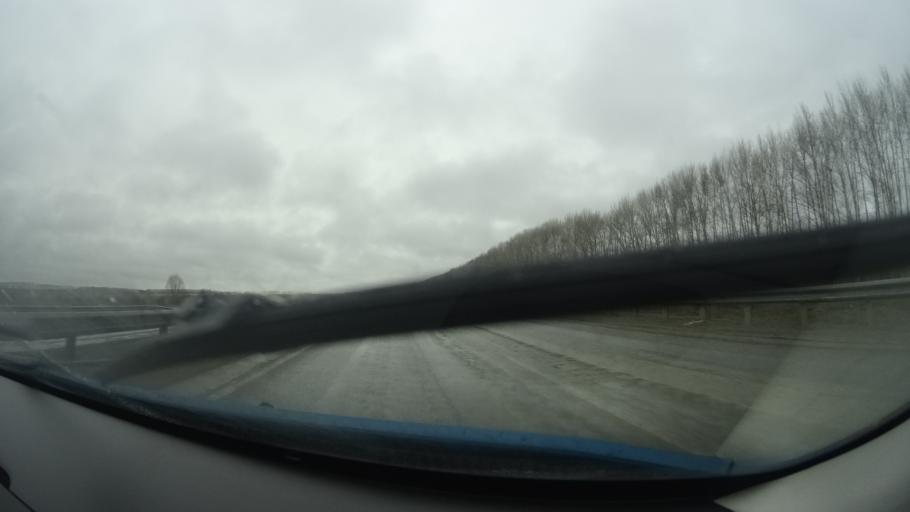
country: RU
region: Bashkortostan
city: Dmitriyevka
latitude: 54.6995
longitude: 55.2610
